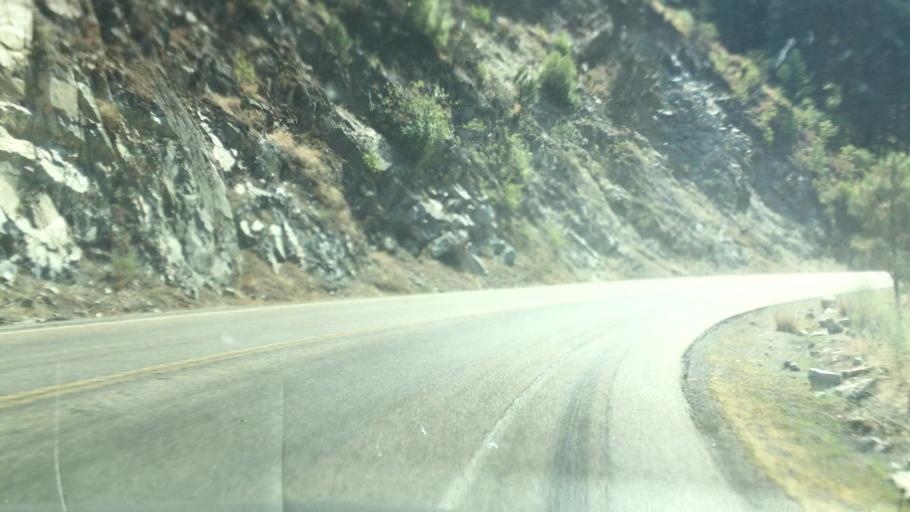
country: US
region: Idaho
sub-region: Boise County
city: Idaho City
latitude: 44.0995
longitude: -116.0958
